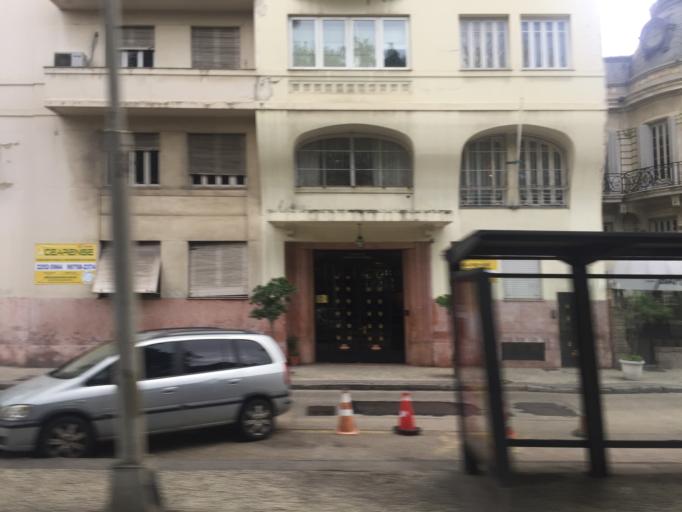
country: BR
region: Rio de Janeiro
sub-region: Rio De Janeiro
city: Rio de Janeiro
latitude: -22.9364
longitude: -43.1742
